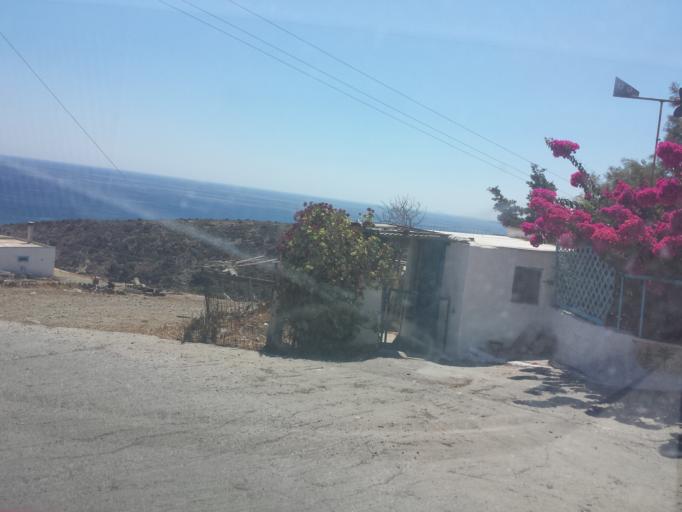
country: GR
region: South Aegean
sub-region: Nomos Kykladon
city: Adamas
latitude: 36.6632
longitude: 24.4148
